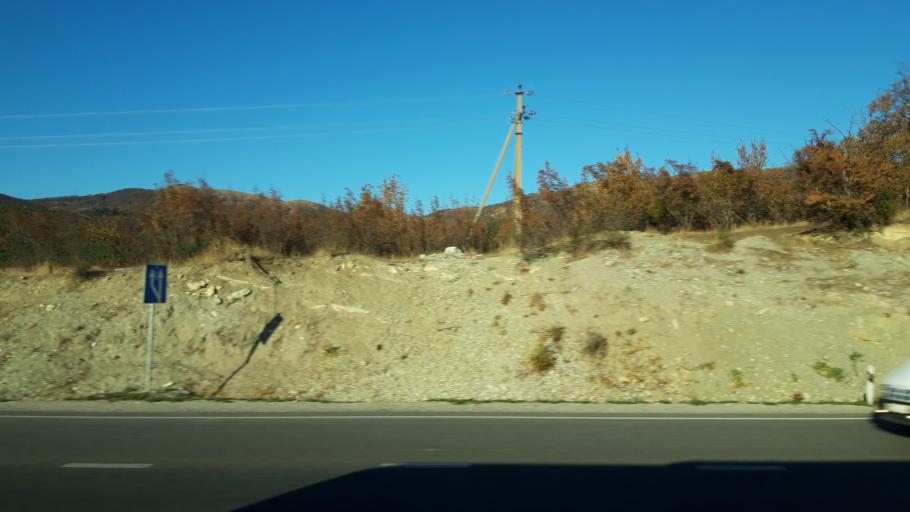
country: RU
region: Krasnodarskiy
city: Kabardinka
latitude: 44.6347
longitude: 37.9956
